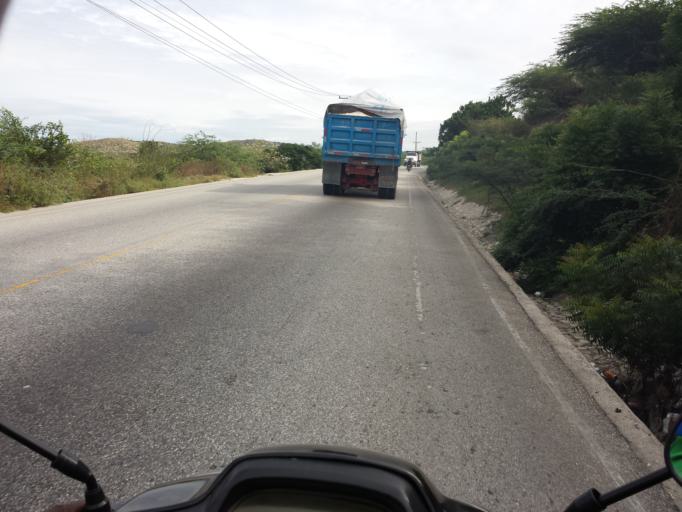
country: HT
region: Artibonite
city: Saint-Marc
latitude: 19.1359
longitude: -72.6747
